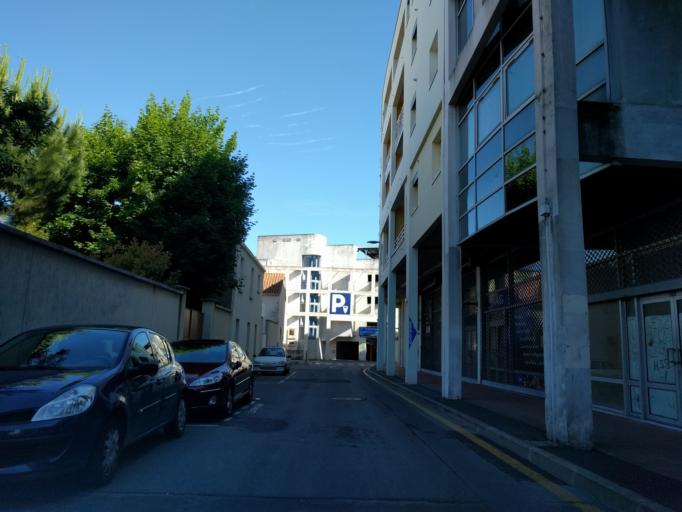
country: FR
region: Poitou-Charentes
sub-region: Departement des Deux-Sevres
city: Niort
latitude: 46.3254
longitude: -0.4565
